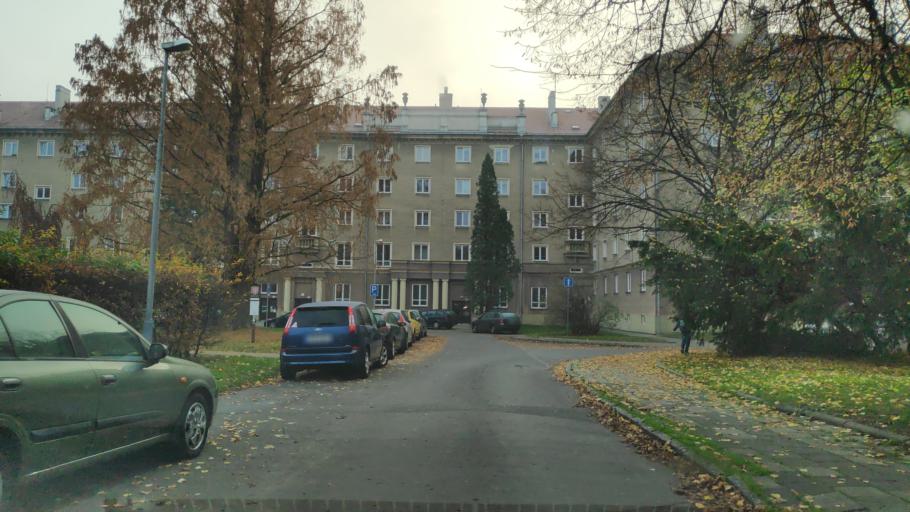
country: CZ
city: Vresina
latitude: 49.8288
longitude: 18.1658
